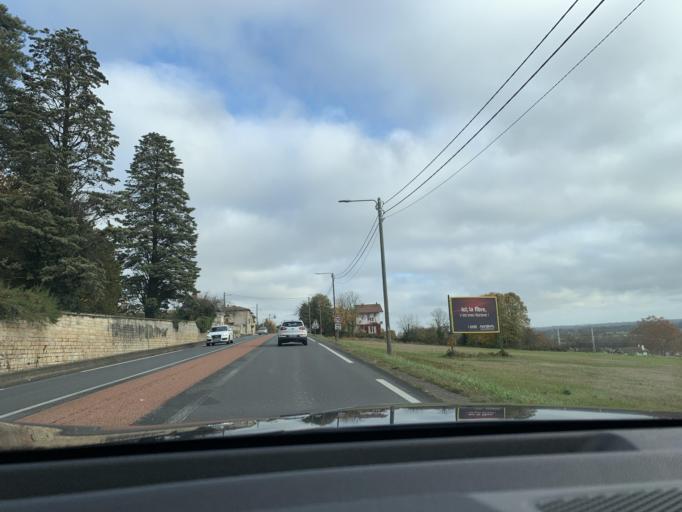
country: FR
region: Bourgogne
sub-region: Departement de Saone-et-Loire
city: Saint-Martin-Belle-Roche
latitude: 46.3638
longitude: 4.8521
